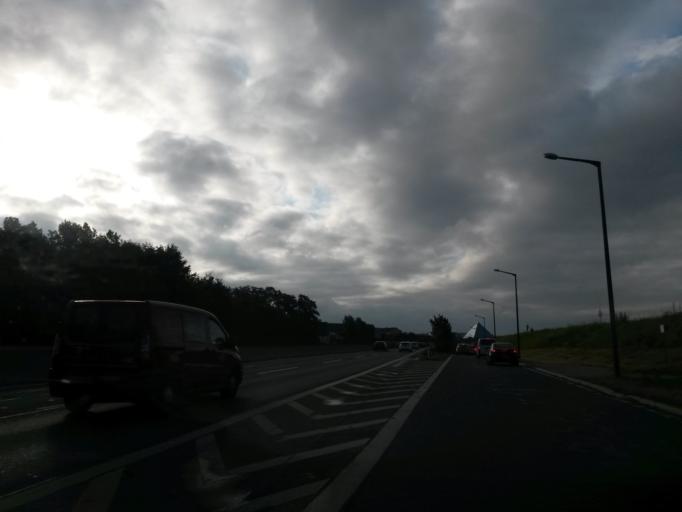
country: DE
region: Bavaria
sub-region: Regierungsbezirk Mittelfranken
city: Furth
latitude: 49.4531
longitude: 10.9859
